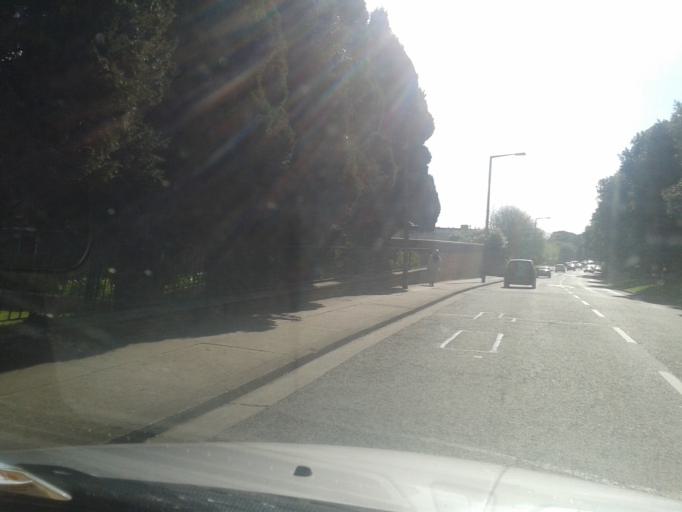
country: IE
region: Leinster
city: Raheny
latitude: 53.3782
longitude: -6.1734
